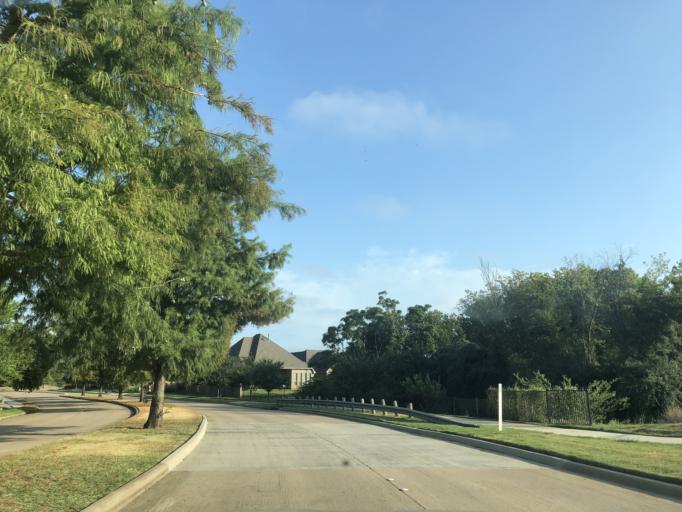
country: US
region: Texas
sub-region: Tarrant County
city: Euless
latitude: 32.8469
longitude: -97.0672
